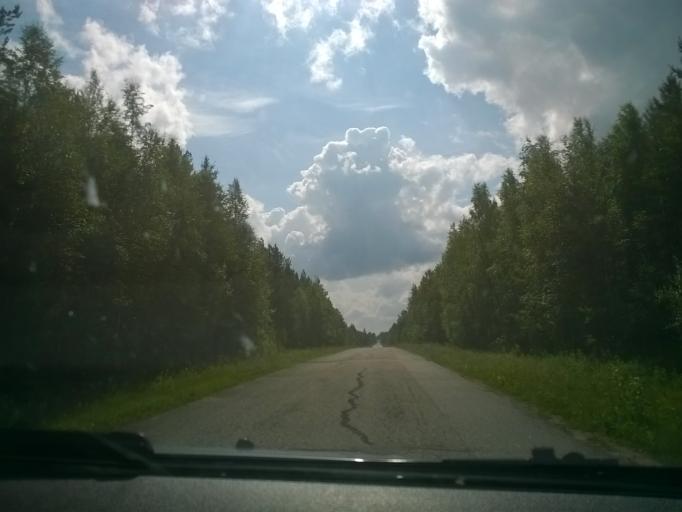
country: FI
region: Kainuu
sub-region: Kehys-Kainuu
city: Kuhmo
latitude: 64.4098
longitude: 29.7695
